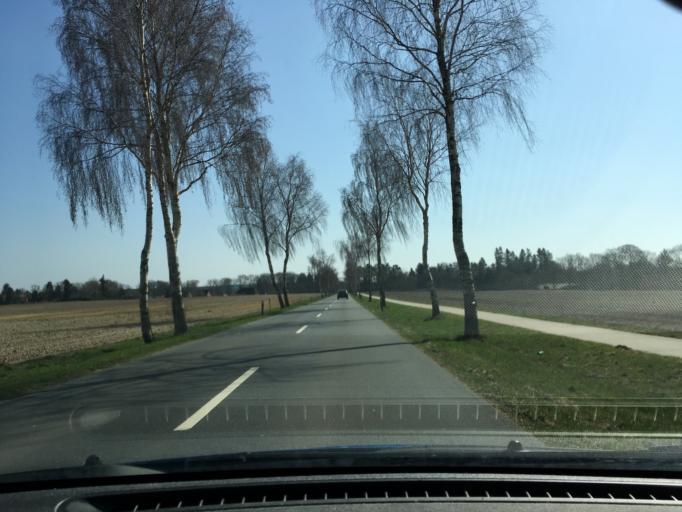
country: DE
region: Lower Saxony
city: Eimke
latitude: 52.9795
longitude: 10.3089
